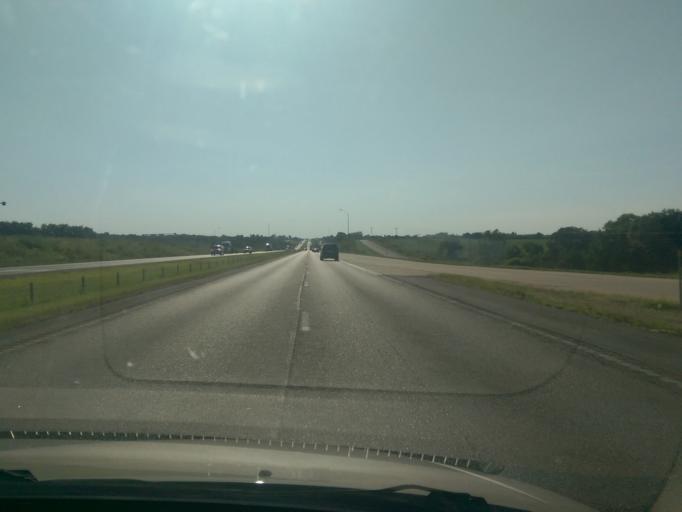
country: US
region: Missouri
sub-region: Lafayette County
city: Odessa
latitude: 39.0045
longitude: -93.8551
